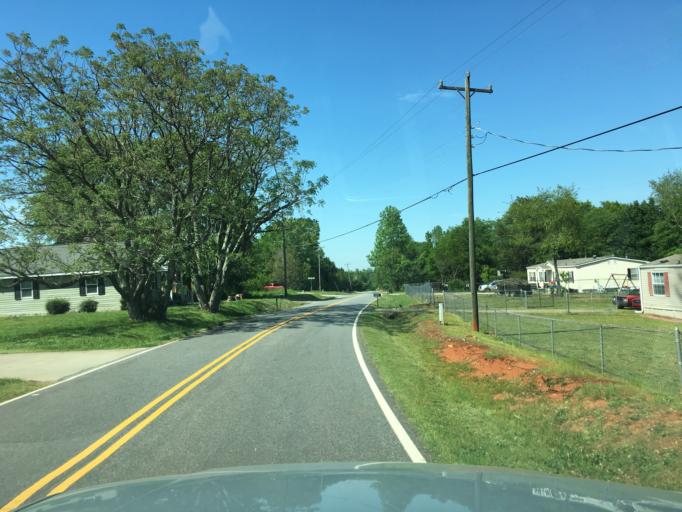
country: US
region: South Carolina
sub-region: Spartanburg County
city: Southern Shops
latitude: 35.0009
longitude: -82.0190
